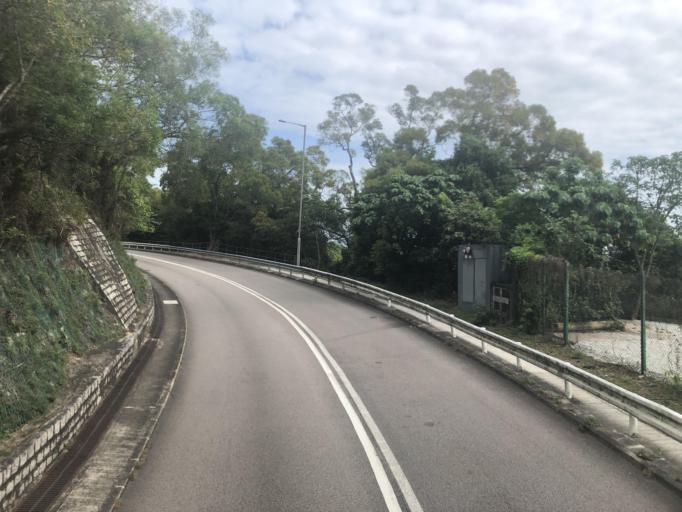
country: HK
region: Sai Kung
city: Sai Kung
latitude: 22.3871
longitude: 114.3035
